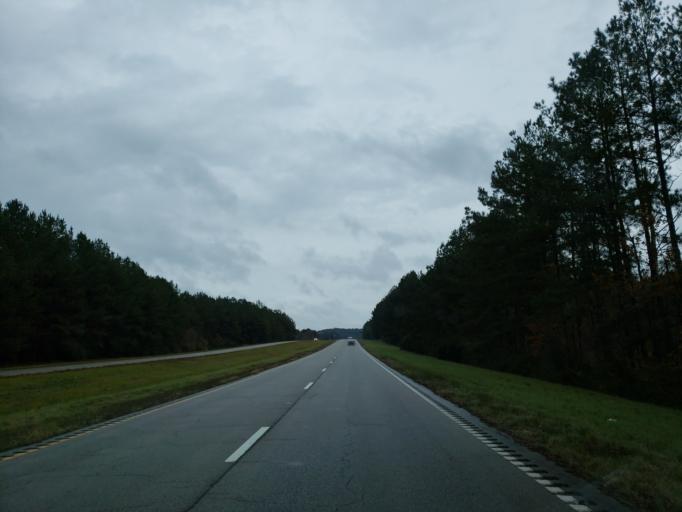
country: US
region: Mississippi
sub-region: Jones County
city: Laurel
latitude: 31.7032
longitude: -89.0828
